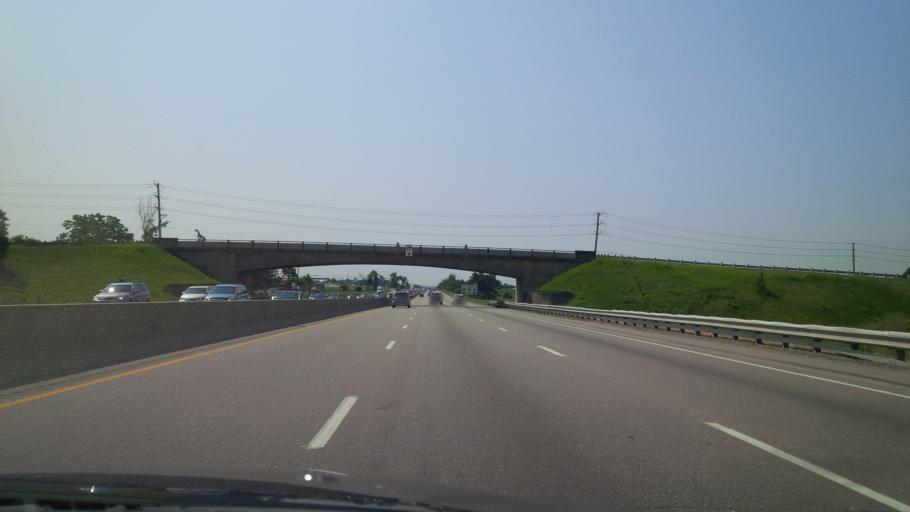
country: CA
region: Ontario
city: Vaughan
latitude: 43.9033
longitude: -79.5621
